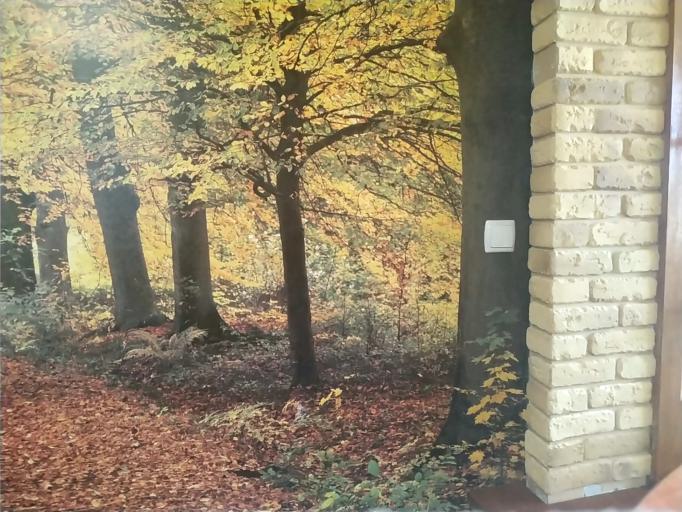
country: RU
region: Tverskaya
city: Vyshniy Volochek
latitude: 57.6700
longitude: 34.5298
